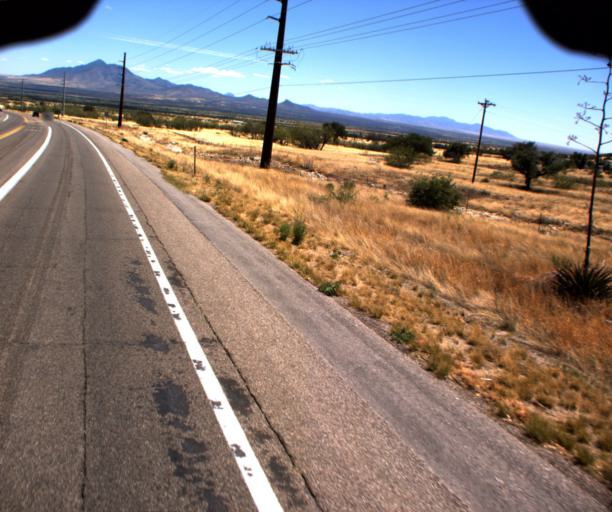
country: US
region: Arizona
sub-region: Cochise County
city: Sierra Vista Southeast
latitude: 31.3821
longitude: -110.2221
